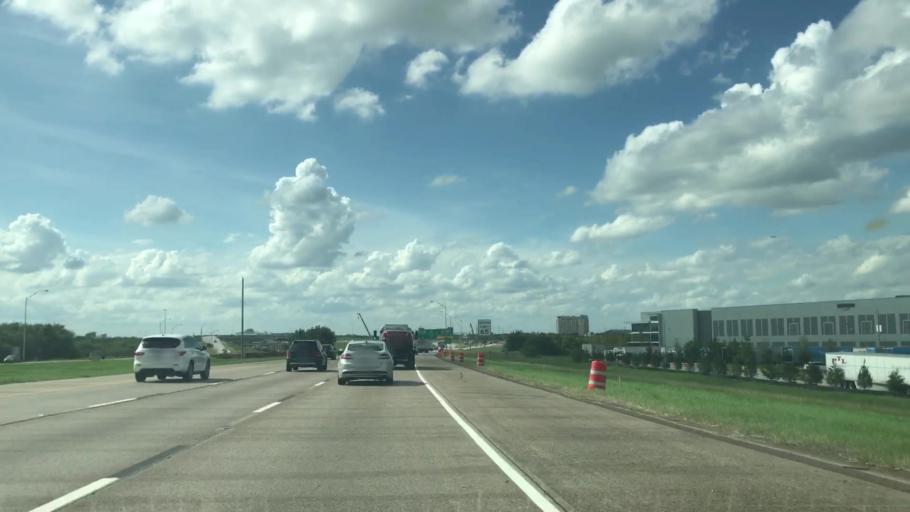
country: US
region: Texas
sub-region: Dallas County
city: Coppell
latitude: 32.9482
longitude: -97.0298
